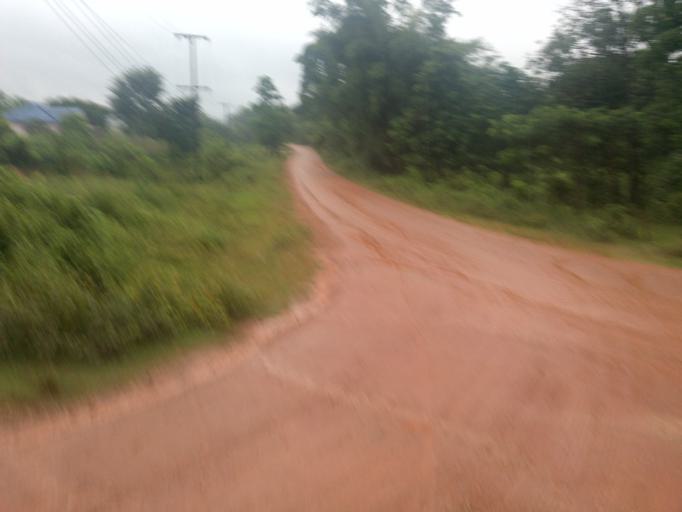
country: LA
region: Bolikhamxai
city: Bolikhan
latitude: 18.5561
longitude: 103.7257
